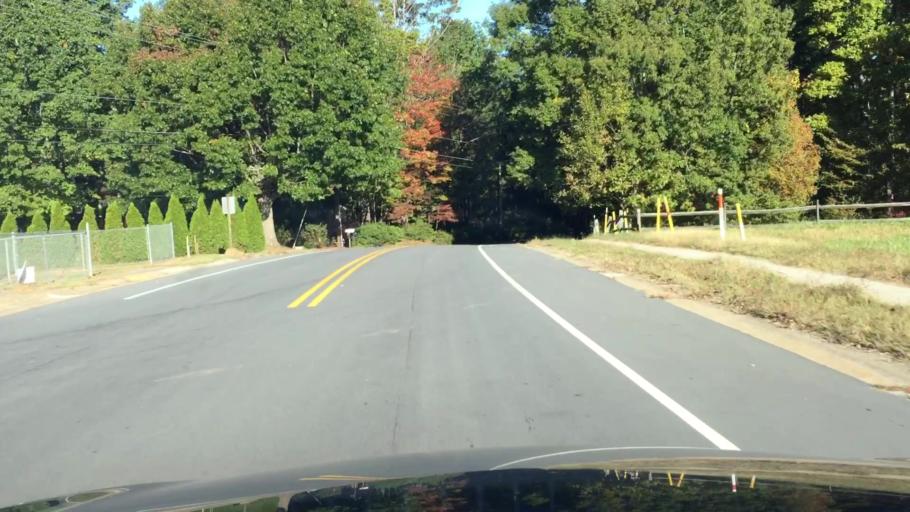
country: US
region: North Carolina
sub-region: Iredell County
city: Mooresville
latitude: 35.5635
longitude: -80.8026
